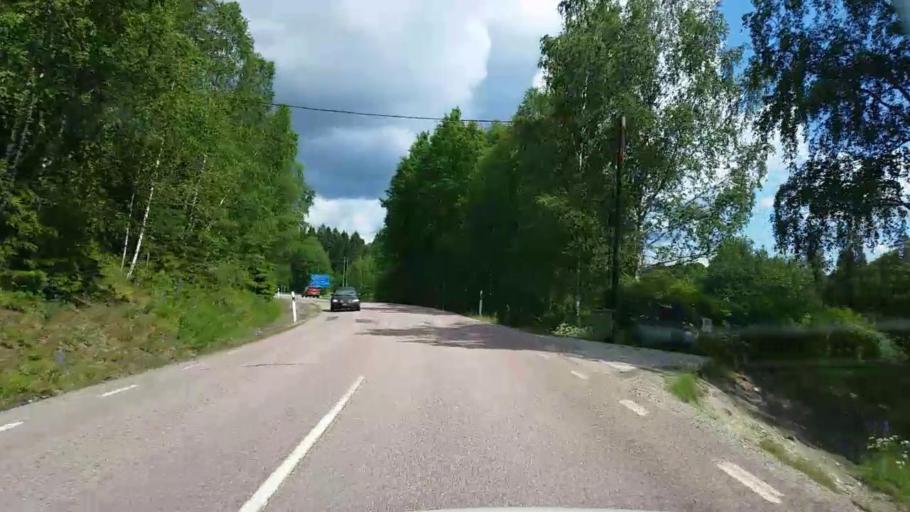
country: SE
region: Vaestmanland
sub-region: Skinnskattebergs Kommun
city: Skinnskatteberg
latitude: 59.8006
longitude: 15.8456
